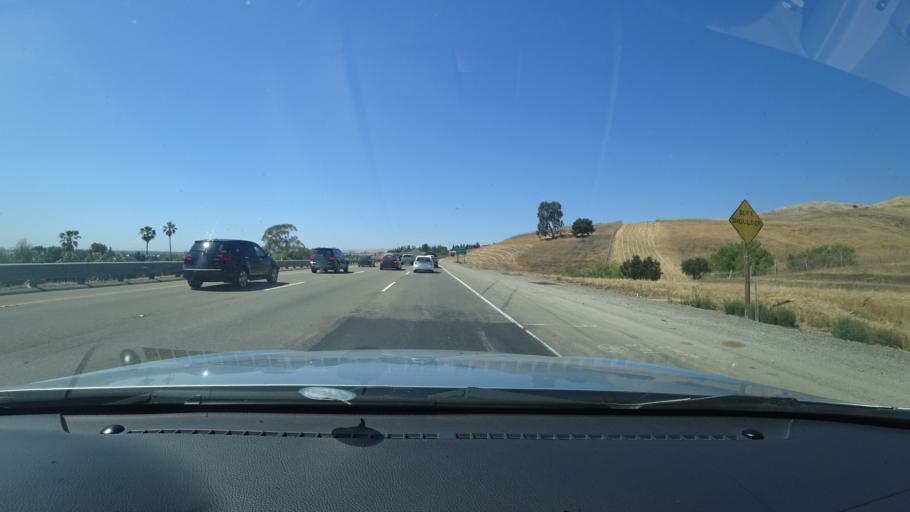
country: US
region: California
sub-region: Santa Clara County
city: Milpitas
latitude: 37.4823
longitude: -121.9132
